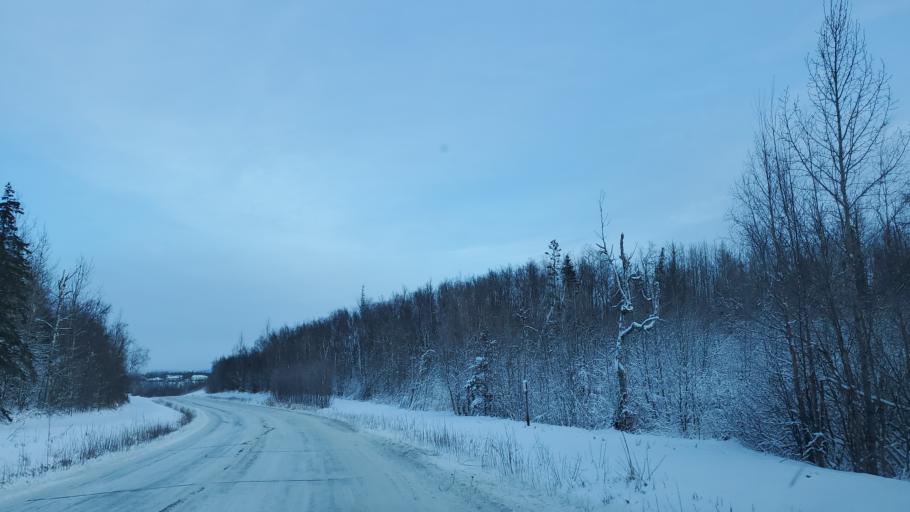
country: US
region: Alaska
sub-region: Matanuska-Susitna Borough
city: Lakes
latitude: 61.5483
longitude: -149.3107
